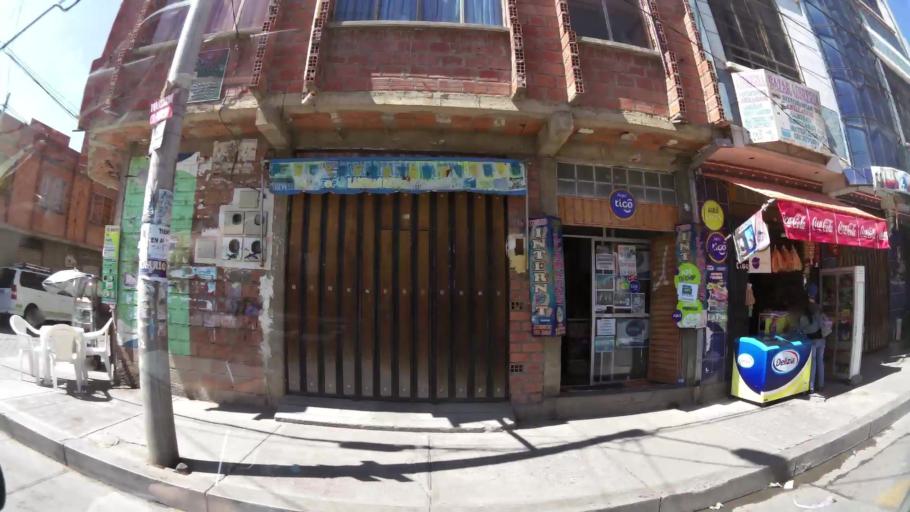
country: BO
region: La Paz
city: La Paz
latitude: -16.5296
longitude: -68.1590
